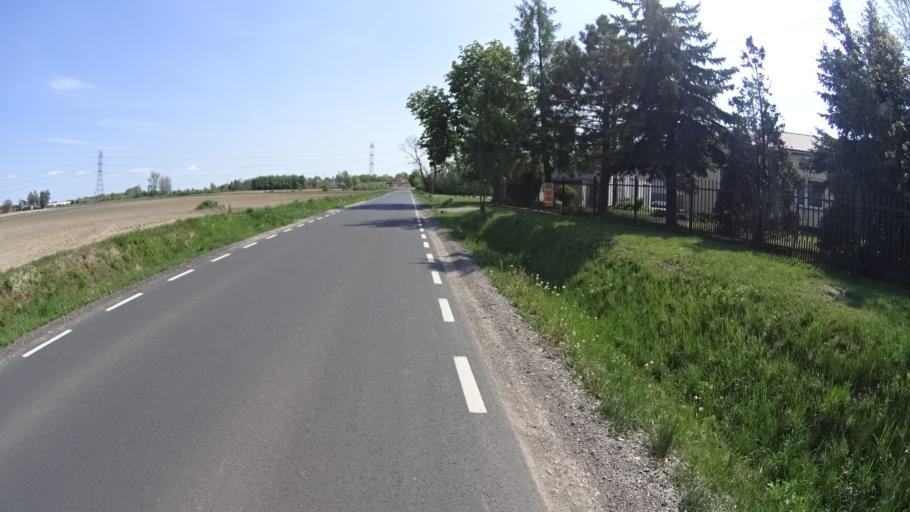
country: PL
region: Masovian Voivodeship
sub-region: Powiat warszawski zachodni
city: Ozarow Mazowiecki
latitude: 52.2359
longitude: 20.7571
